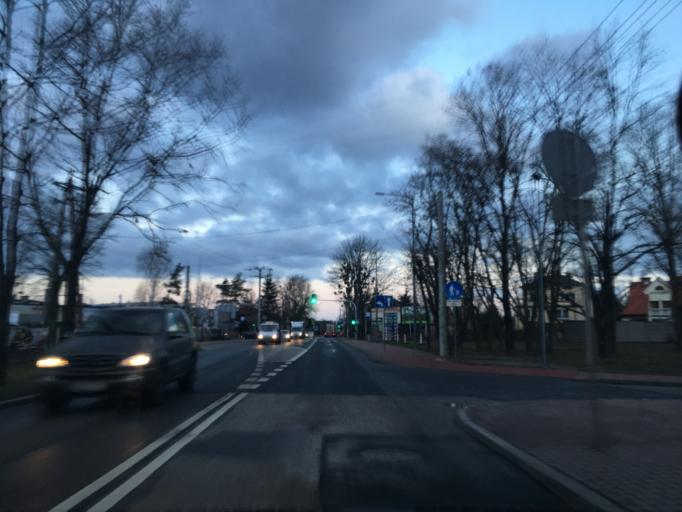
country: PL
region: Masovian Voivodeship
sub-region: Powiat grodziski
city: Grodzisk Mazowiecki
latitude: 52.0995
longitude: 20.6456
